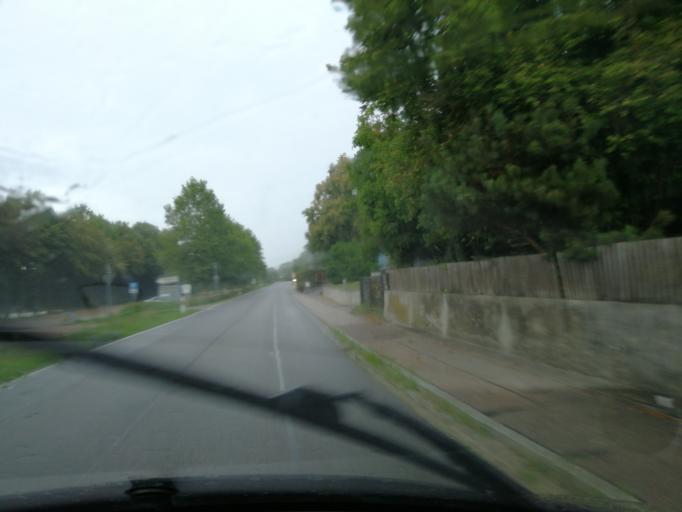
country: DE
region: Bavaria
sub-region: Upper Palatinate
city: Altenthann
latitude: 49.0205
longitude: 12.2858
